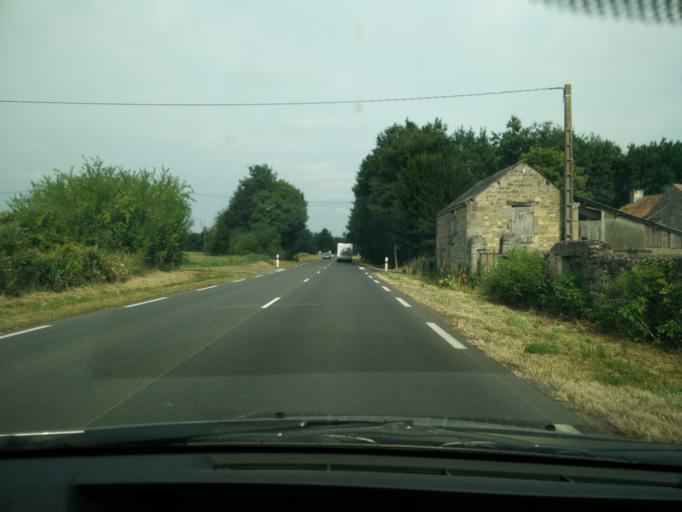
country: FR
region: Pays de la Loire
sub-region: Departement de Maine-et-Loire
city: Vaudelnay
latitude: 47.1546
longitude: -0.1837
